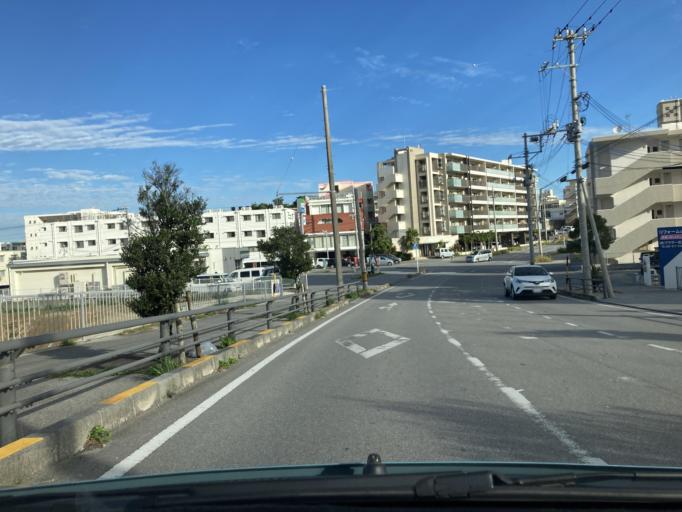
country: JP
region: Okinawa
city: Ginowan
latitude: 26.2331
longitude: 127.7243
